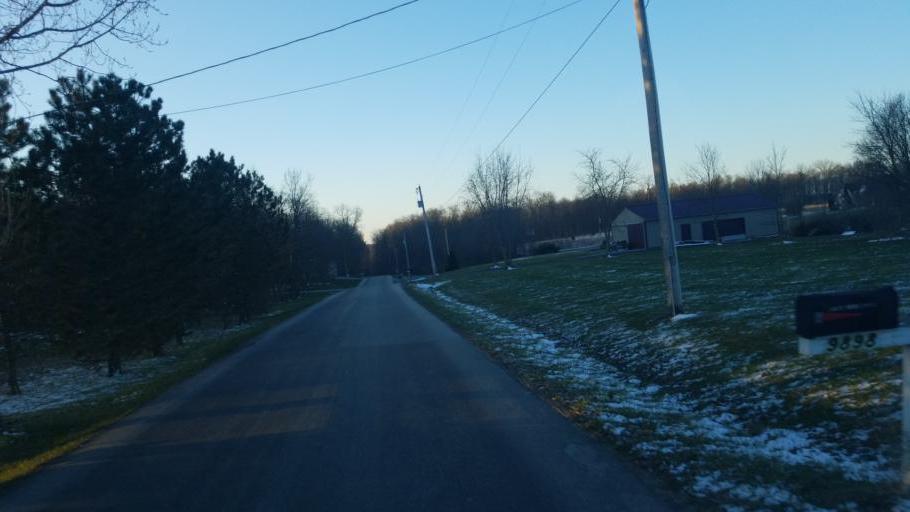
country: US
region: Ohio
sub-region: Highland County
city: Leesburg
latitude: 39.2835
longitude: -83.5034
